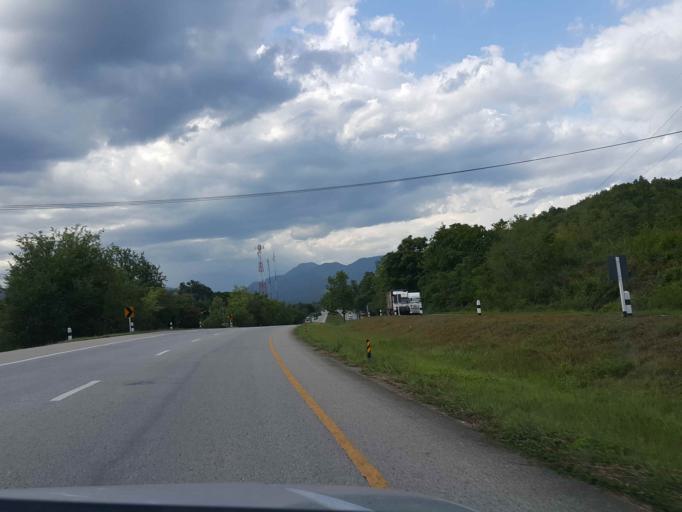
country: TH
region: Lampang
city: Thoen
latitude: 17.7096
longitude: 99.2296
